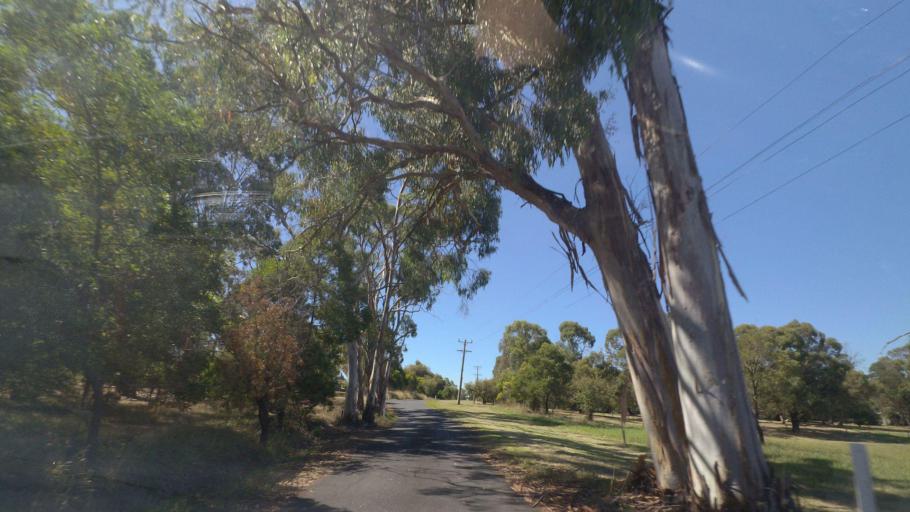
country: AU
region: Victoria
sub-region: Yarra Ranges
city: Chirnside Park
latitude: -37.7407
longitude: 145.3286
